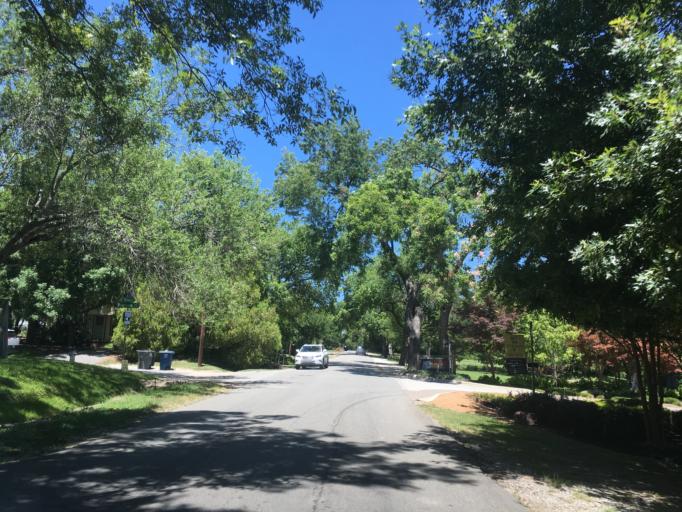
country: US
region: Texas
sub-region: Dallas County
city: Highland Park
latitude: 32.8443
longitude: -96.7078
